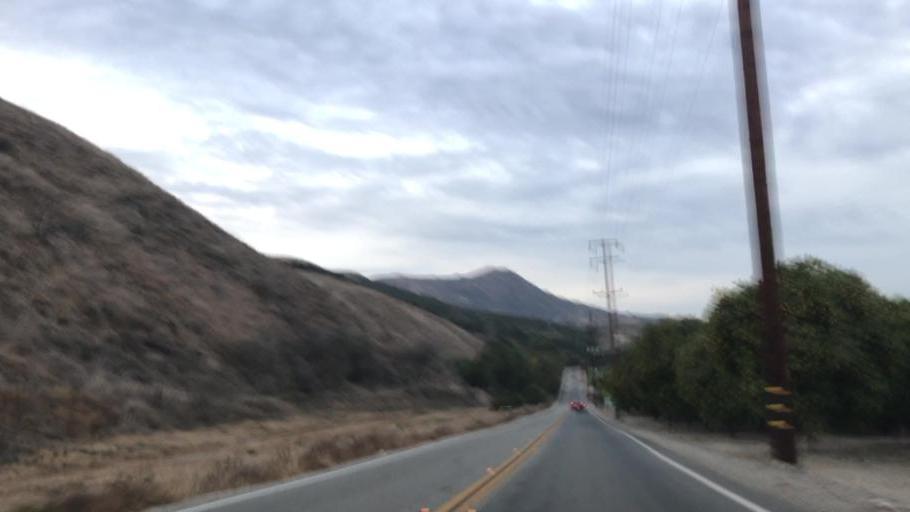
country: US
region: California
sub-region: Ventura County
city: Fillmore
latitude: 34.3572
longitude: -118.9627
